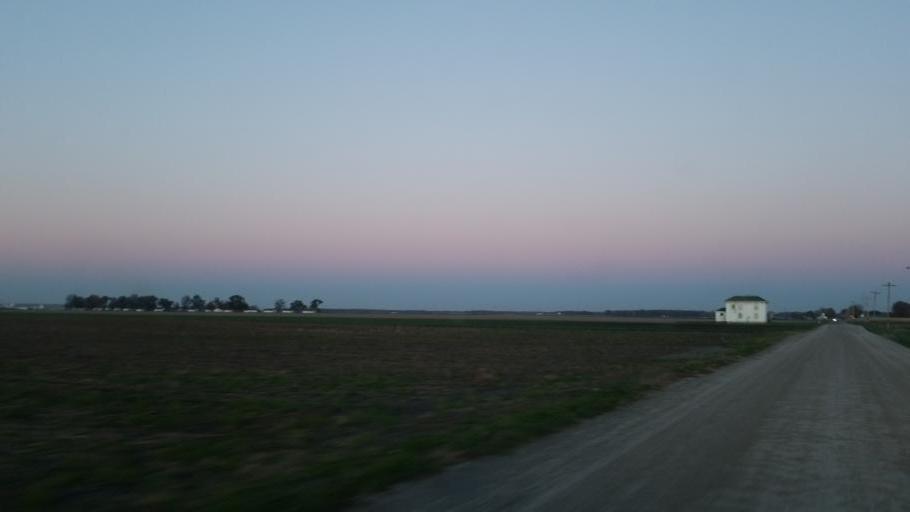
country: US
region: Ohio
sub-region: Huron County
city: Willard
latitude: 40.9957
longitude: -82.7478
